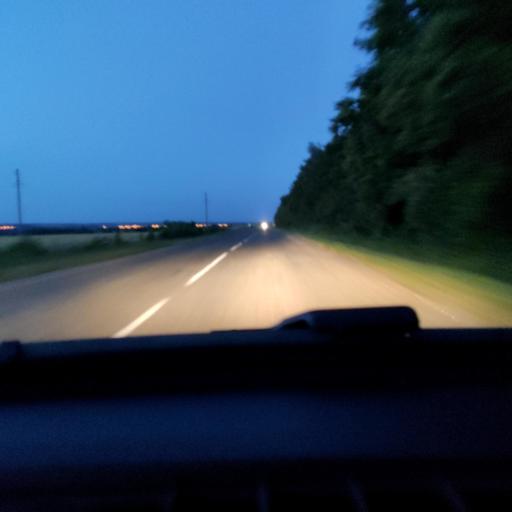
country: RU
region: Lipetsk
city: Zadonsk
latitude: 52.3099
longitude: 38.8857
